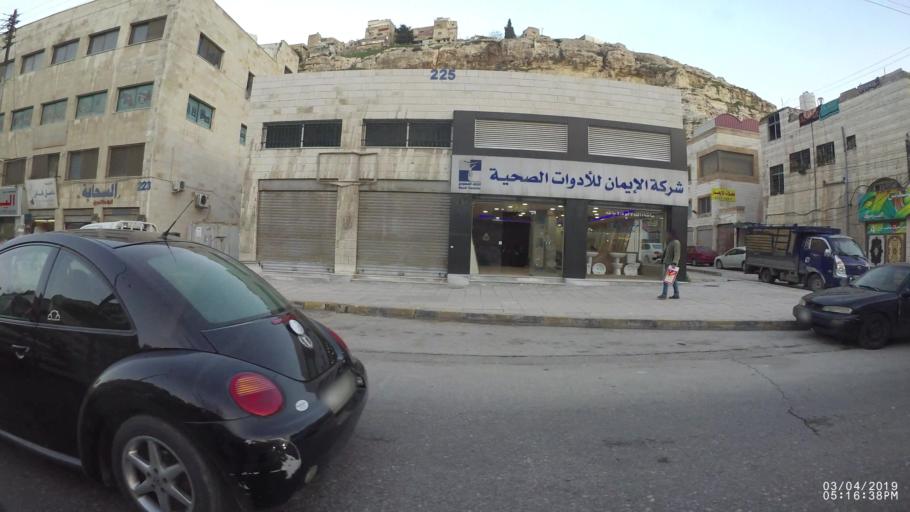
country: JO
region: Amman
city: Amman
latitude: 31.9328
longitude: 35.9220
